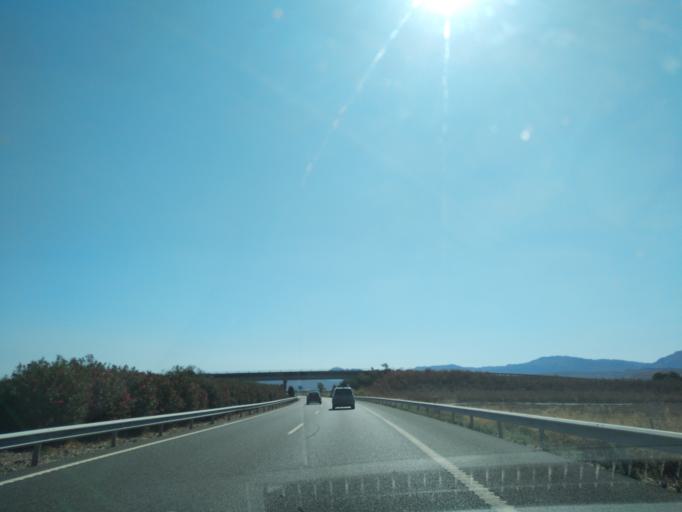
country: ES
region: Andalusia
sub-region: Provincia de Malaga
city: Mollina
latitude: 37.0844
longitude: -4.6202
